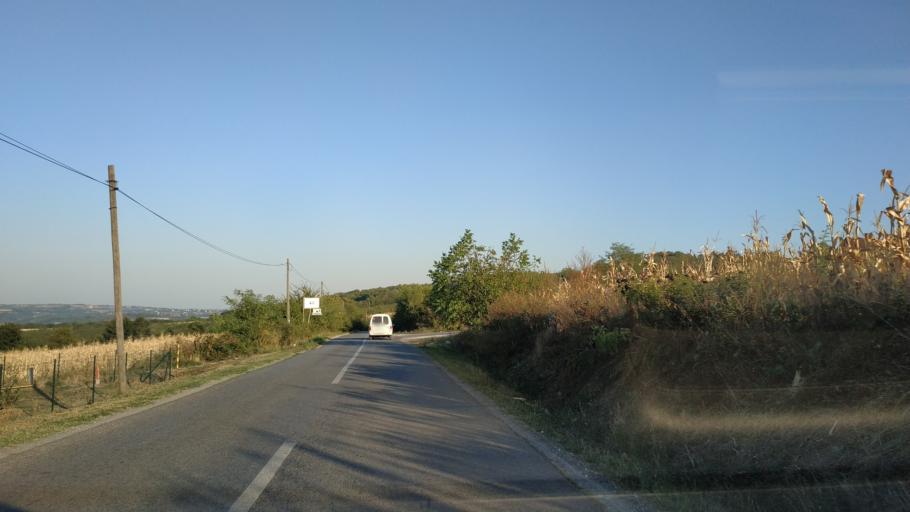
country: RS
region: Central Serbia
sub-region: Sumadijski Okrug
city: Topola
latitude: 44.2726
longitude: 20.6379
